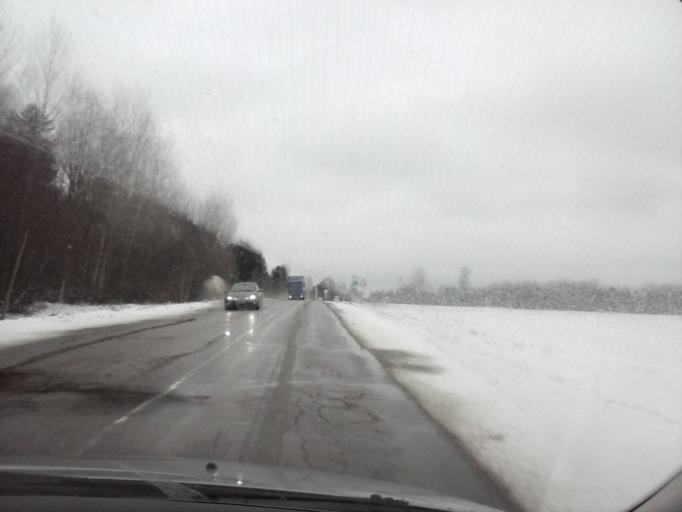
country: LV
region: Valkas Rajons
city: Valka
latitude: 57.7567
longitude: 25.9819
